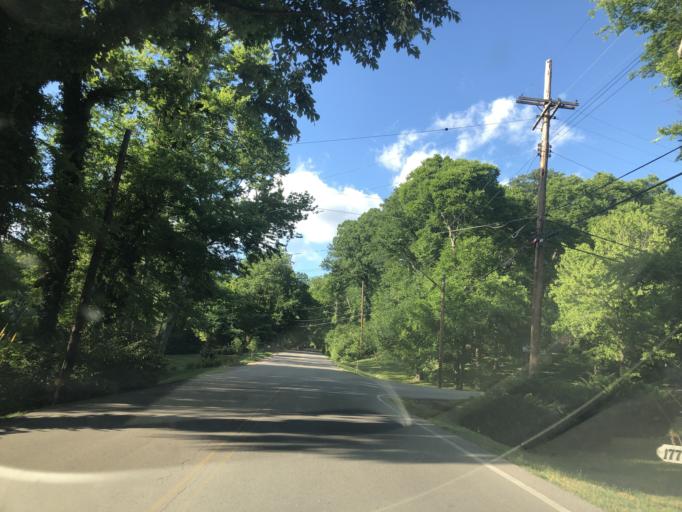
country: US
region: Tennessee
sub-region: Davidson County
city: Forest Hills
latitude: 36.0718
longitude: -86.8261
